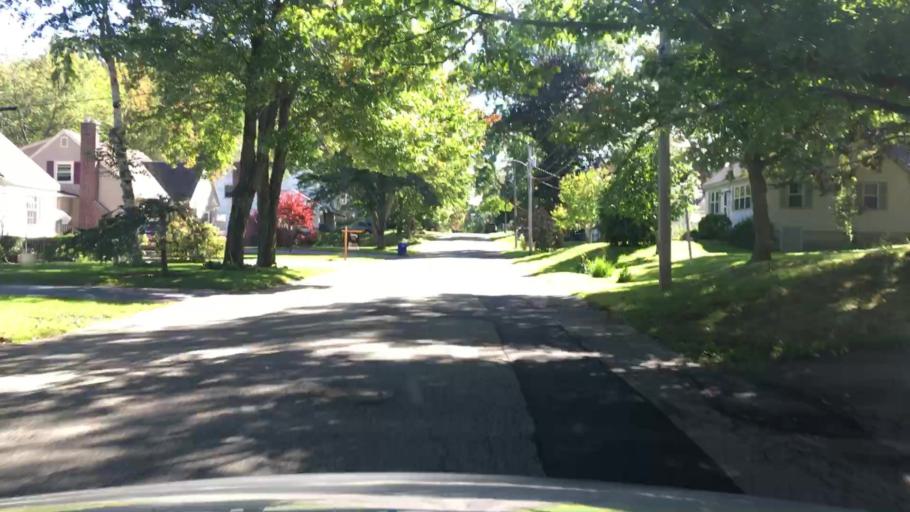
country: US
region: Maine
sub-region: Cumberland County
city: Westbrook
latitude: 43.6745
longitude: -70.3575
